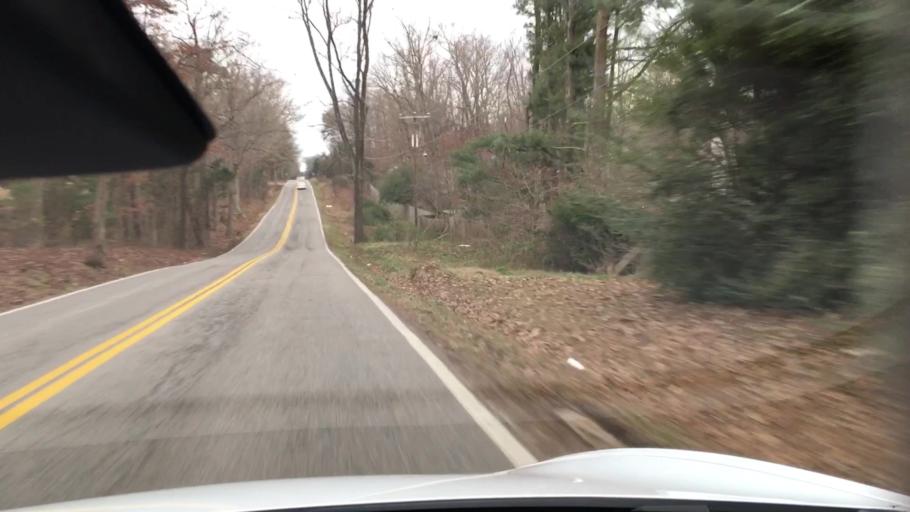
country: US
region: Virginia
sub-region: Chesterfield County
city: Bon Air
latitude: 37.5199
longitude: -77.5730
